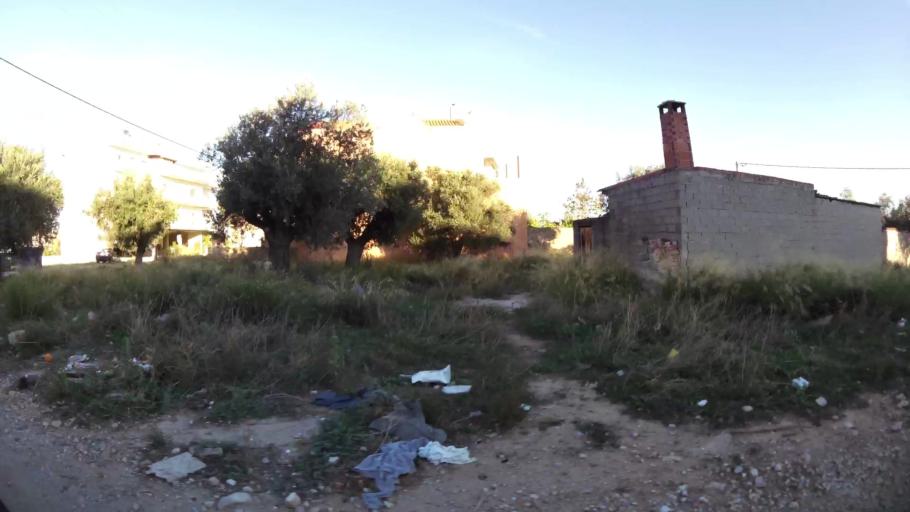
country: GR
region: Attica
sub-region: Nomarchia Anatolikis Attikis
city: Spata
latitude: 37.9585
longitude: 23.9233
